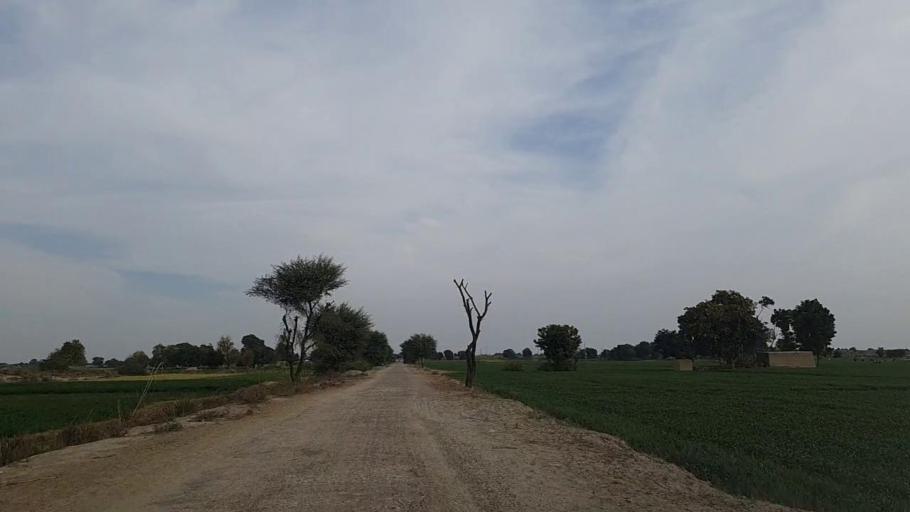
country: PK
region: Sindh
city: Jam Sahib
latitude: 26.4403
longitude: 68.5859
